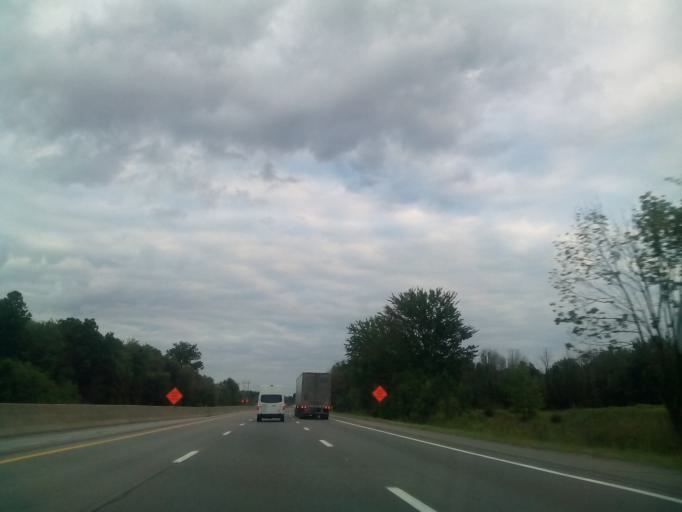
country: US
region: Ohio
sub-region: Trumbull County
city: Newton Falls
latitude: 41.1773
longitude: -80.9218
